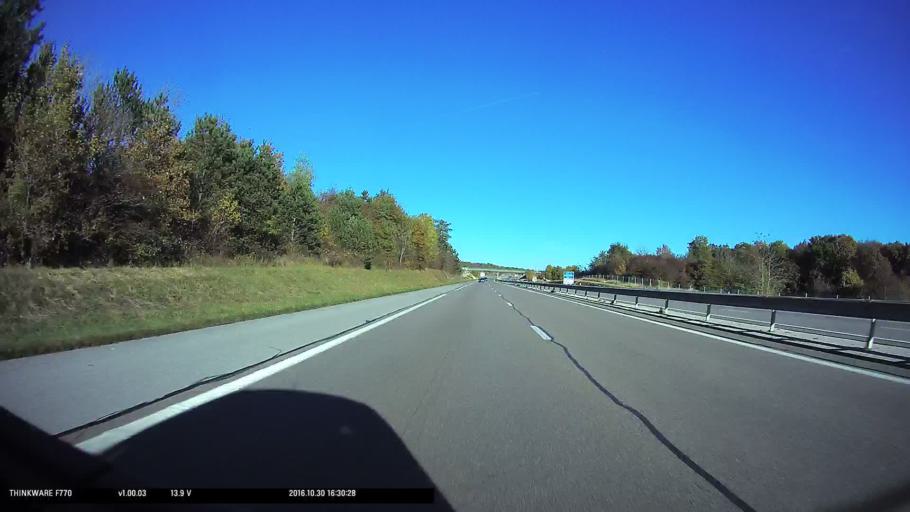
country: FR
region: Franche-Comte
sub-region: Departement du Doubs
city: Roulans
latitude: 47.3417
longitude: 6.2384
